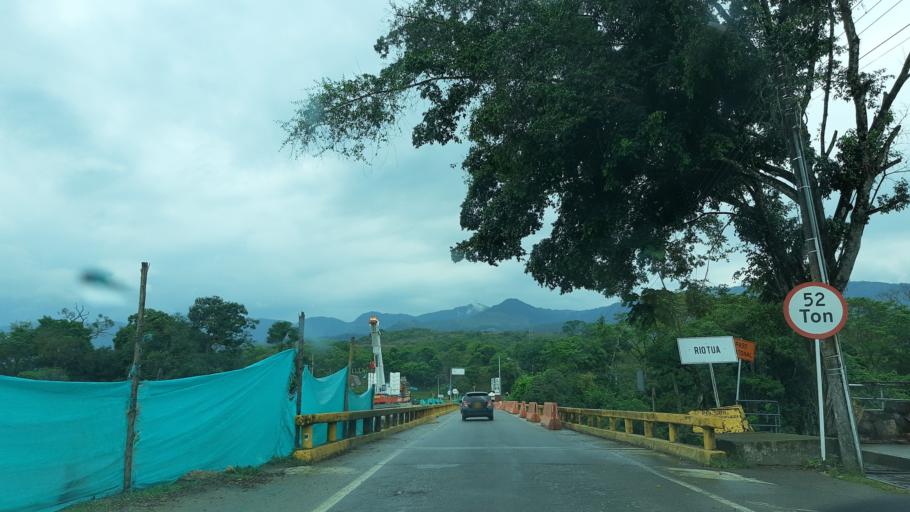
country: CO
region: Casanare
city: Monterrey
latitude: 4.8854
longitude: -72.8999
